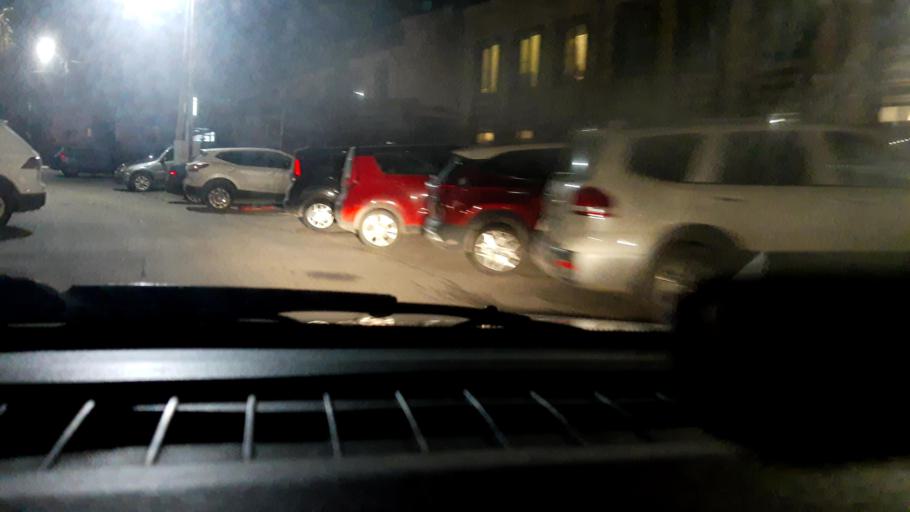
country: RU
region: Nizjnij Novgorod
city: Afonino
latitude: 56.2824
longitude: 44.0614
